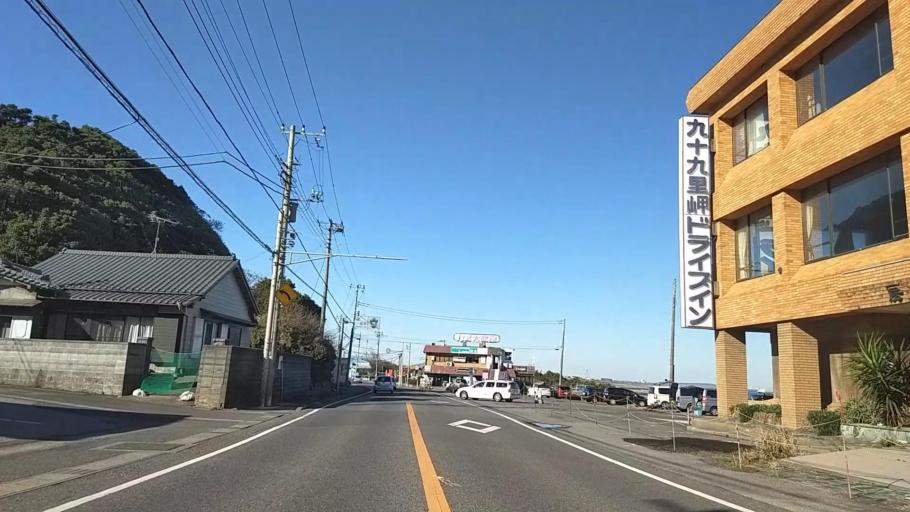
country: JP
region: Chiba
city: Ohara
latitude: 35.3296
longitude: 140.3968
